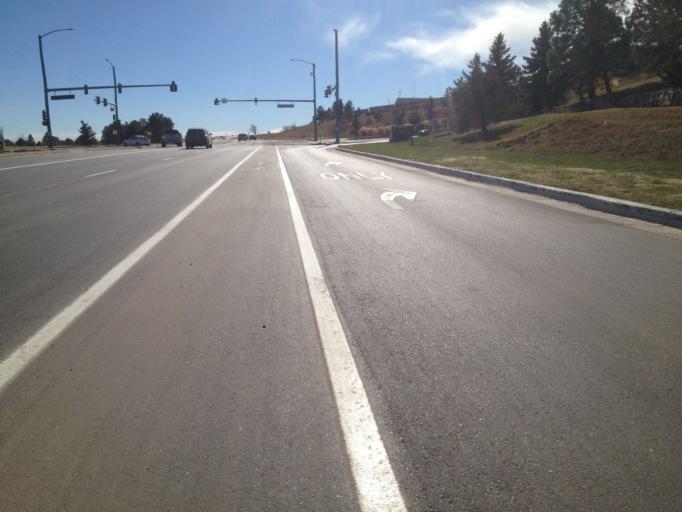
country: US
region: Colorado
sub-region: Boulder County
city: Superior
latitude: 39.9459
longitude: -105.1640
